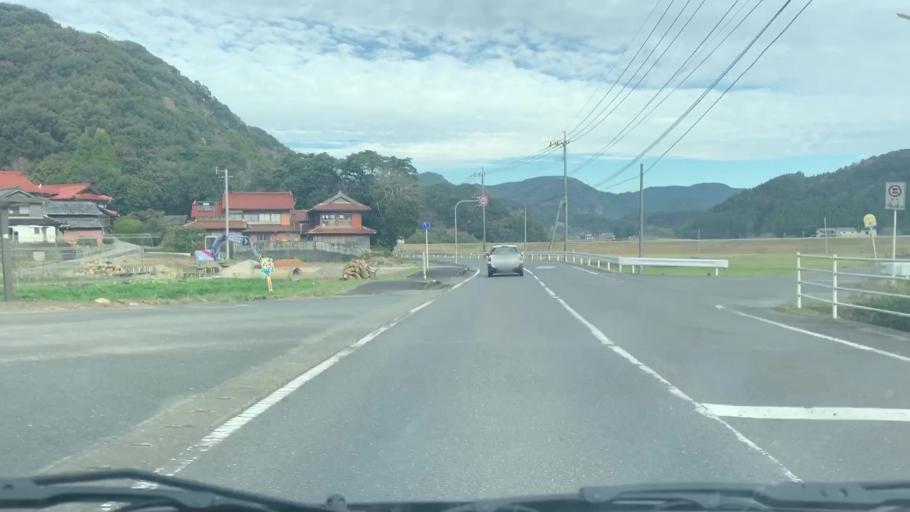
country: JP
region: Saga Prefecture
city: Imaricho-ko
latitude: 33.3147
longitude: 129.9705
